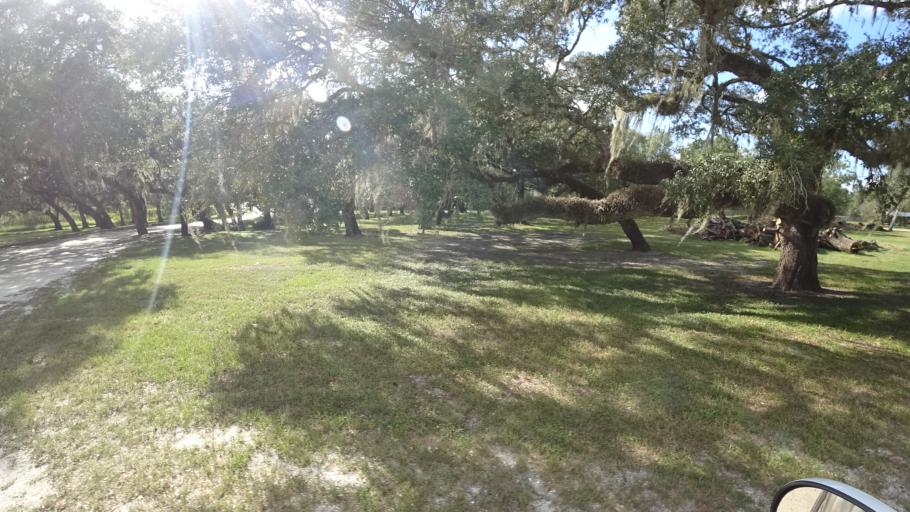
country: US
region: Florida
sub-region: Sarasota County
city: Lake Sarasota
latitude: 27.3454
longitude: -82.1569
